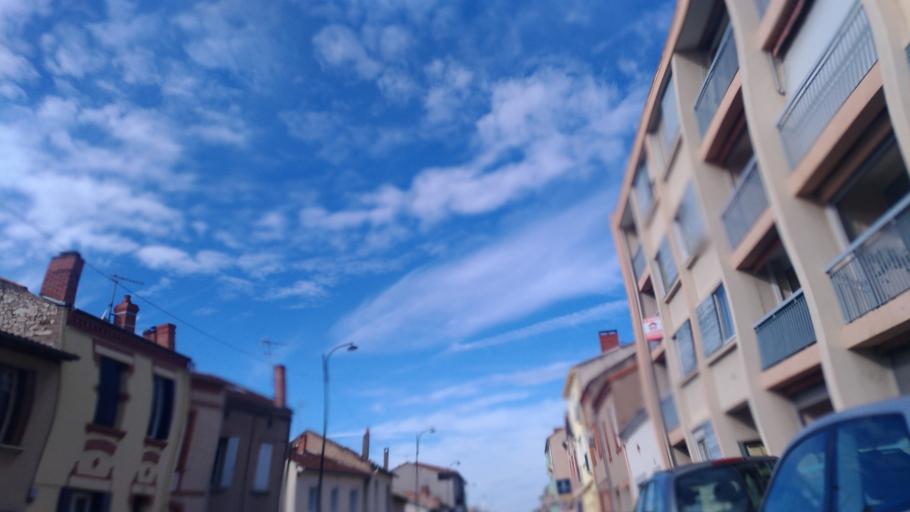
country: FR
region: Midi-Pyrenees
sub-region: Departement du Tarn
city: Albi
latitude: 43.9229
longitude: 2.1604
